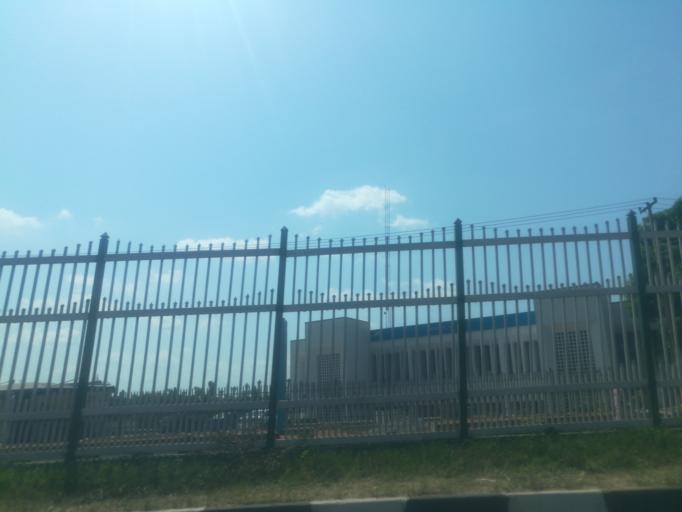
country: NG
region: Ogun
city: Abeokuta
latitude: 7.1330
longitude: 3.3320
